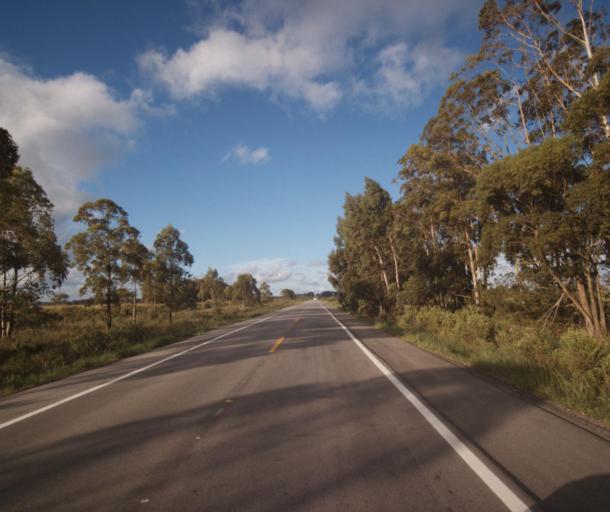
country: BR
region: Rio Grande do Sul
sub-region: Rio Grande
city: Rio Grande
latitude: -32.1346
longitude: -52.3743
